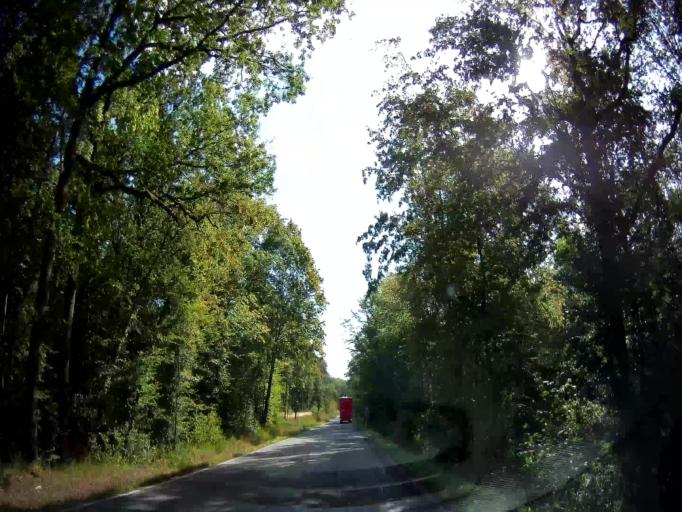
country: BE
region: Wallonia
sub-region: Province de Namur
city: Rochefort
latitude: 50.1675
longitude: 5.1728
